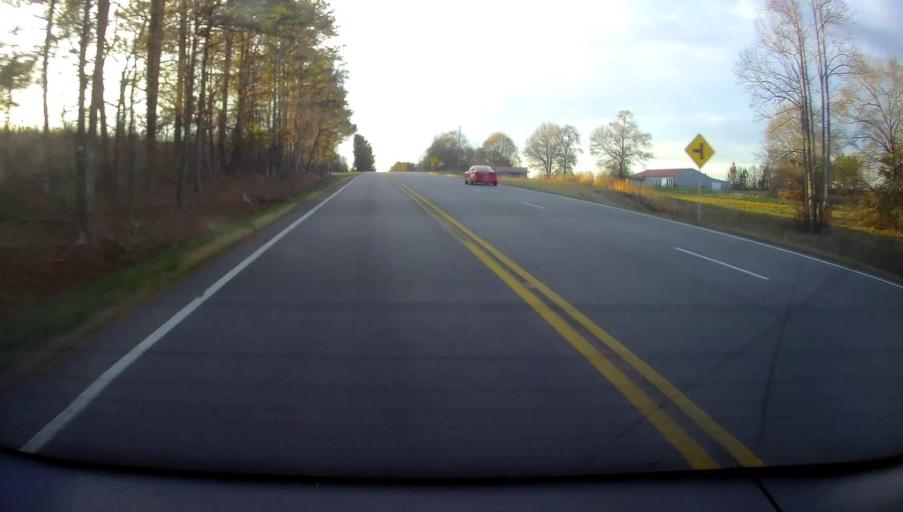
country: US
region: Alabama
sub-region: Etowah County
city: Attalla
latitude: 34.0512
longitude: -86.1850
